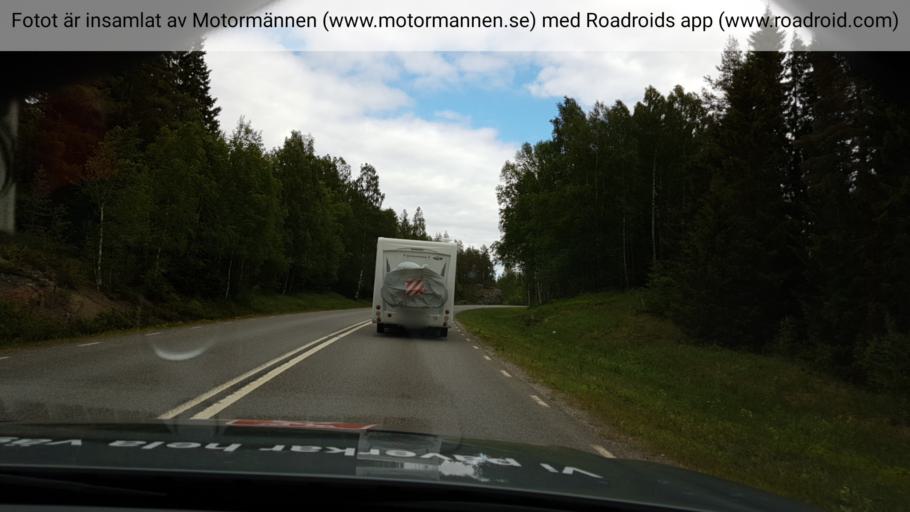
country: SE
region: Jaemtland
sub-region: Stroemsunds Kommun
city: Stroemsund
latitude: 64.3222
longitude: 15.1996
